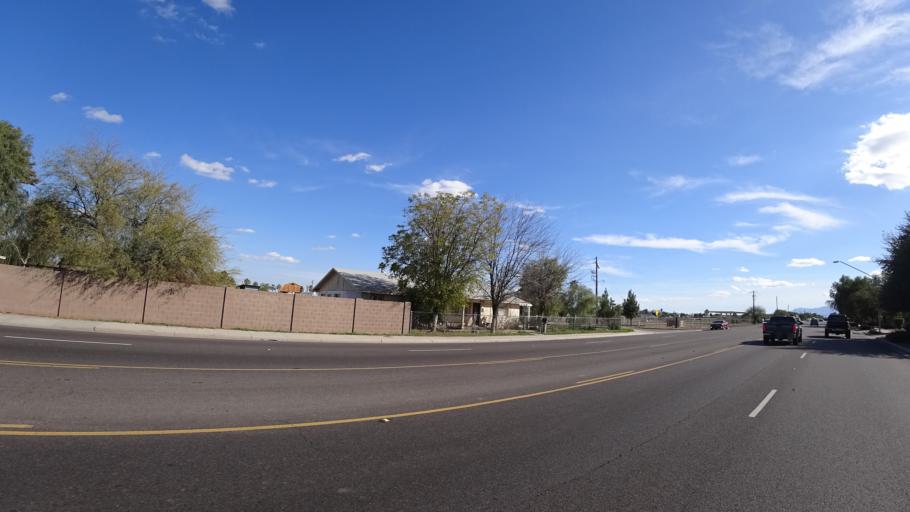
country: US
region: Arizona
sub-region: Maricopa County
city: Glendale
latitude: 33.5295
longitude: -112.2206
